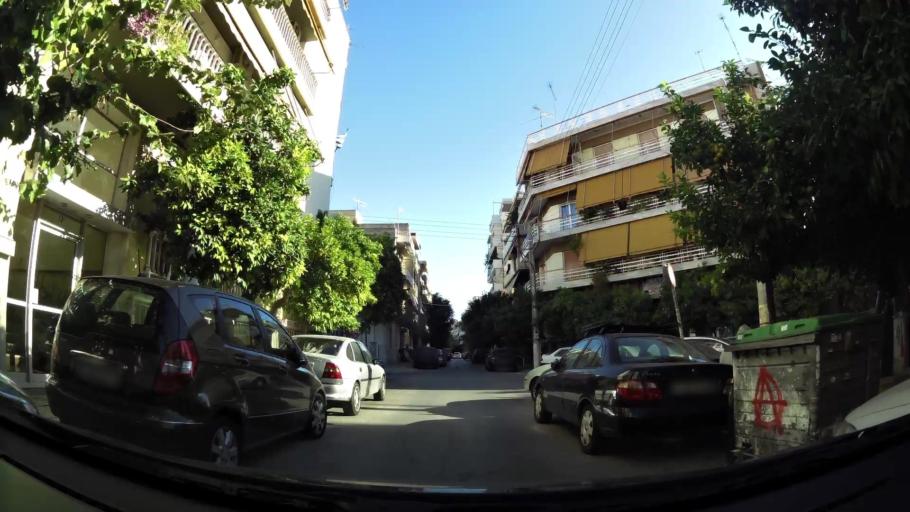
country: GR
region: Attica
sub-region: Nomos Piraios
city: Nikaia
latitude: 37.9768
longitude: 23.6568
